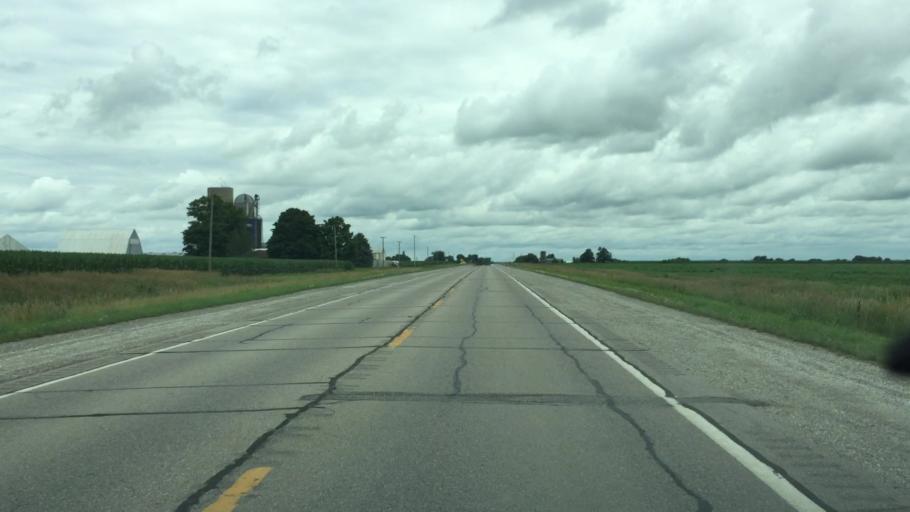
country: US
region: Iowa
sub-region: Jasper County
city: Monroe
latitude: 41.5524
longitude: -93.0971
